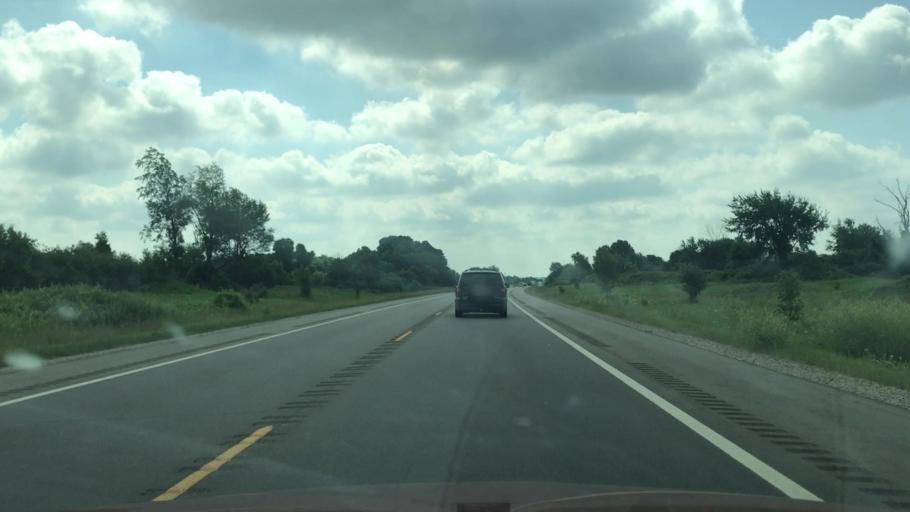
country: US
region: Michigan
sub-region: Kent County
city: Kent City
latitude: 43.2254
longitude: -85.7765
